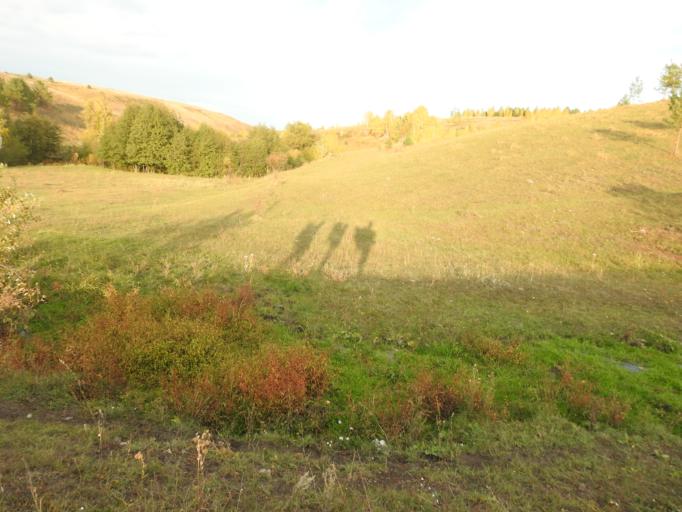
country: RU
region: Saratov
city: Baltay
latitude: 52.5638
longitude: 46.6670
